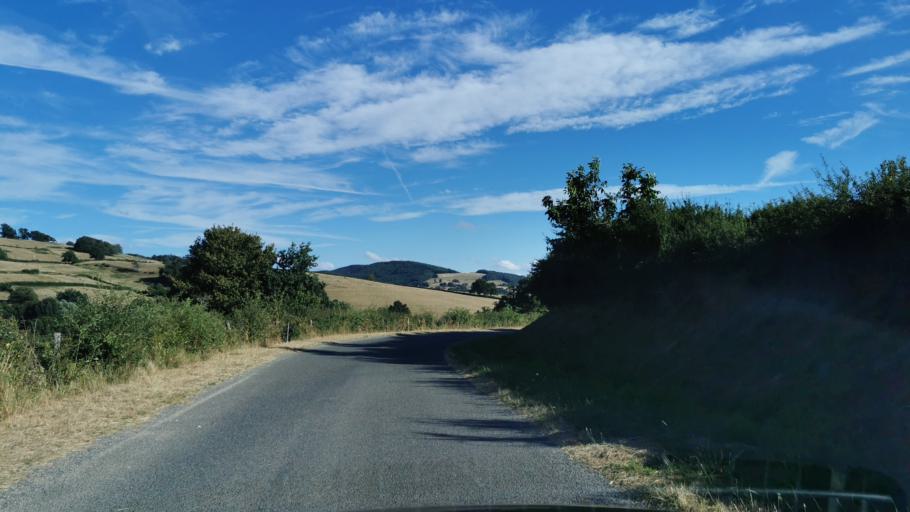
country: FR
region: Bourgogne
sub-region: Departement de Saone-et-Loire
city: Marmagne
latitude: 46.8661
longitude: 4.3141
